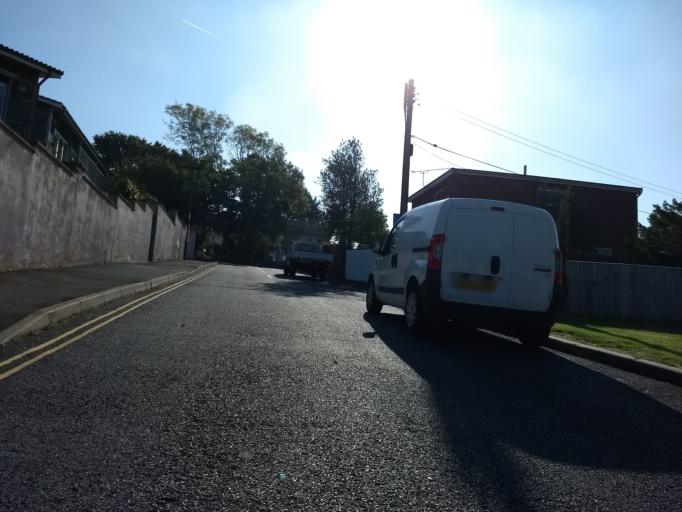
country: GB
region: England
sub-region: Isle of Wight
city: Newchurch
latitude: 50.7253
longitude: -1.2239
